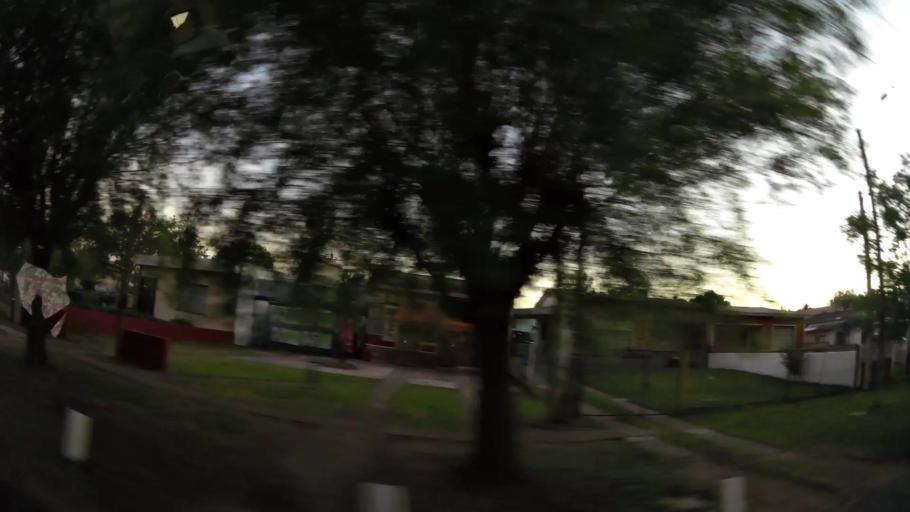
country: UY
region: Canelones
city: Toledo
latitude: -34.8086
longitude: -56.1380
